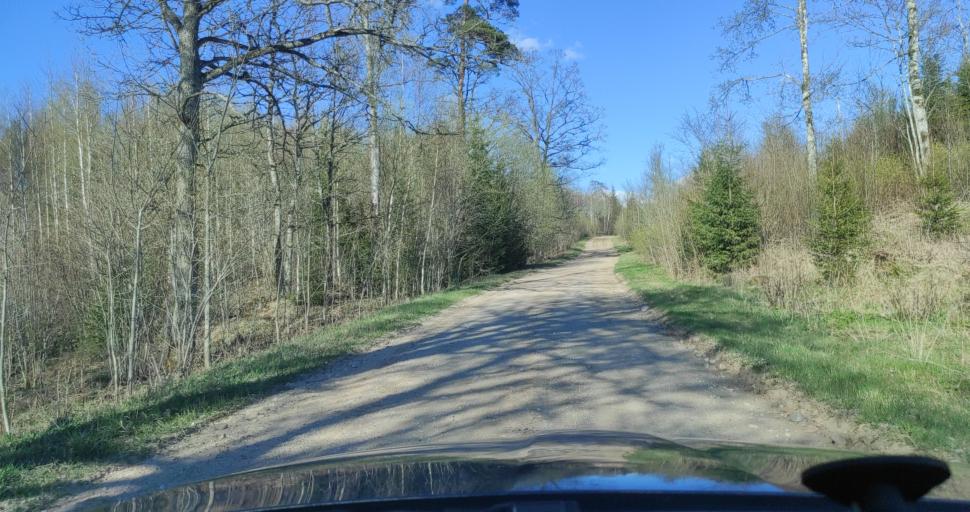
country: LV
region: Kuldigas Rajons
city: Kuldiga
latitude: 56.8845
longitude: 21.8340
